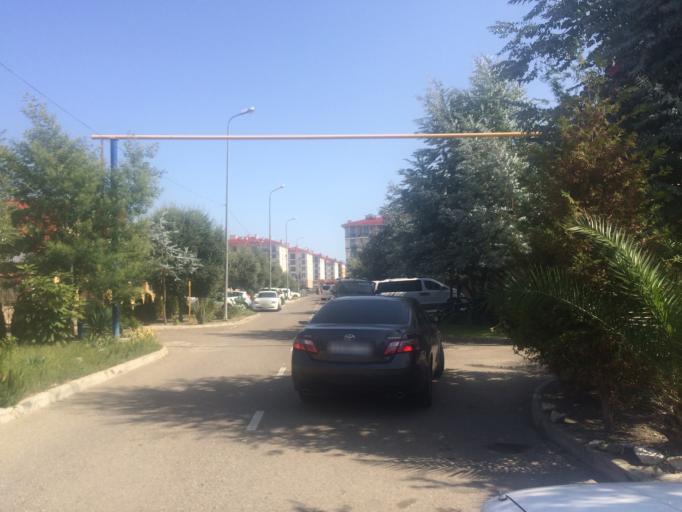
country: RU
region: Krasnodarskiy
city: Adler
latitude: 43.3980
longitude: 39.9733
